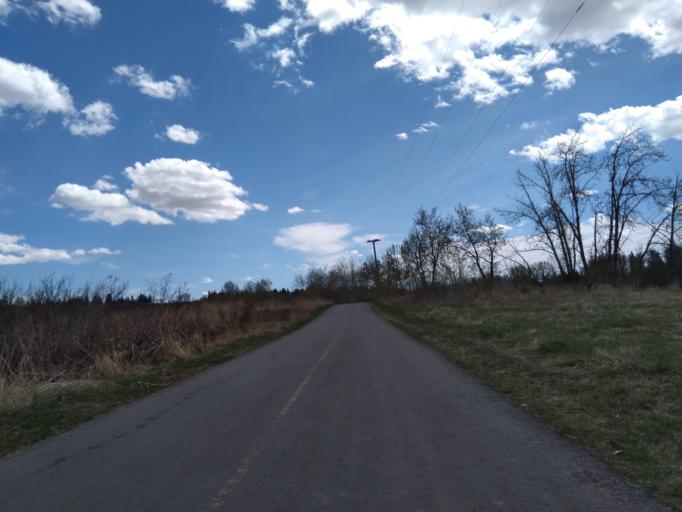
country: CA
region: Alberta
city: Calgary
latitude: 51.0879
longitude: -114.1758
